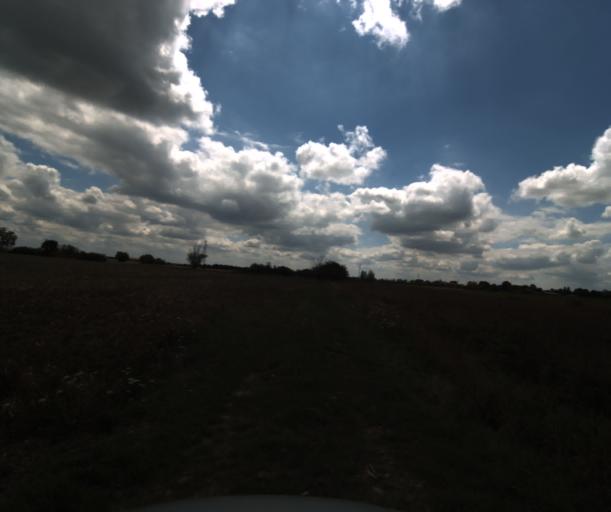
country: FR
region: Midi-Pyrenees
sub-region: Departement de la Haute-Garonne
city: Lacasse
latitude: 43.4215
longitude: 1.2525
